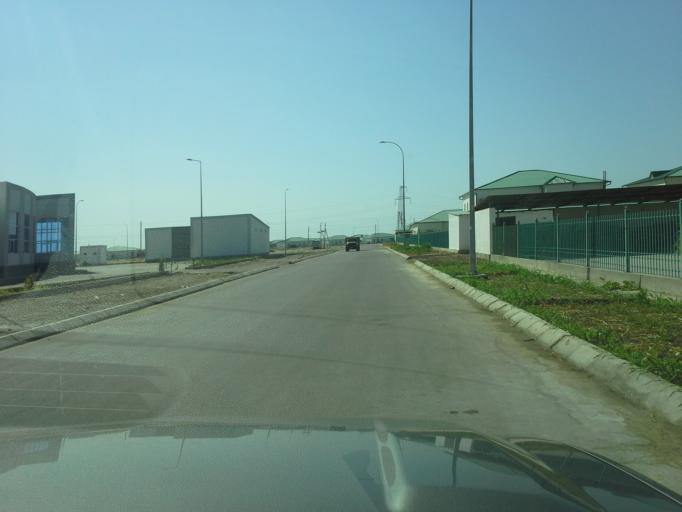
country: TM
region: Dasoguz
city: Dasoguz
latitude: 41.8046
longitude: 59.9512
